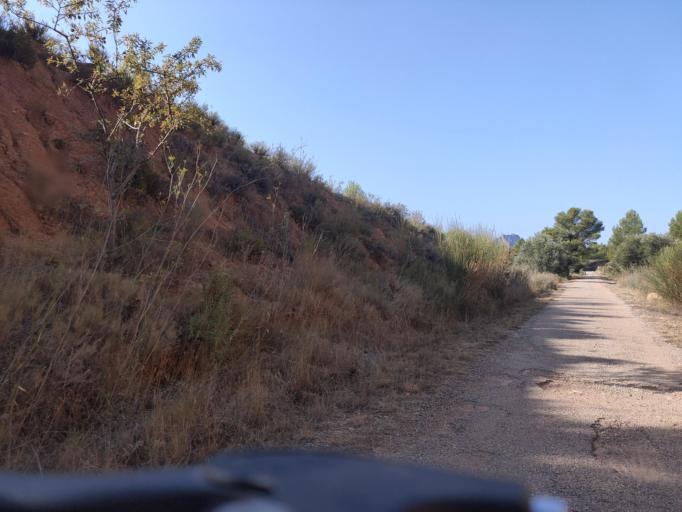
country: ES
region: Catalonia
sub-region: Provincia de Tarragona
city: Bot
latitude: 41.0023
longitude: 0.3742
